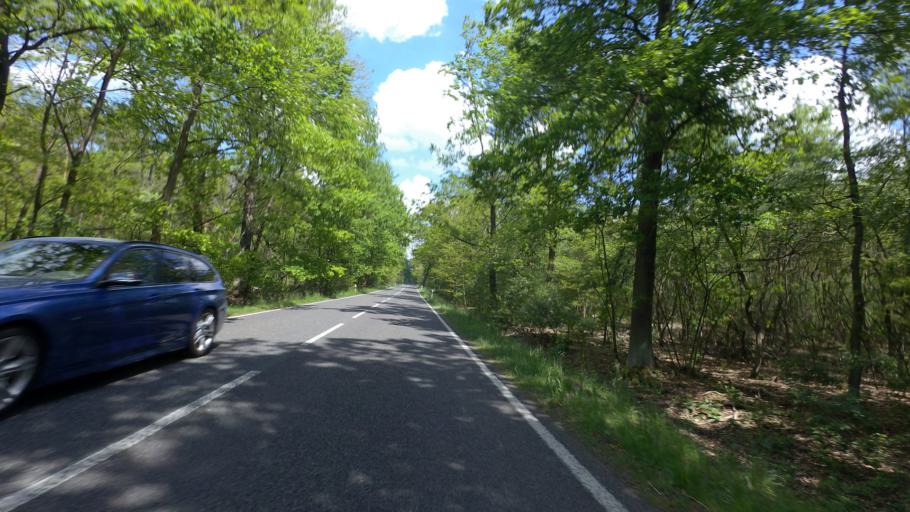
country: DE
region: Brandenburg
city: Straupitz
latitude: 51.9451
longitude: 14.1755
